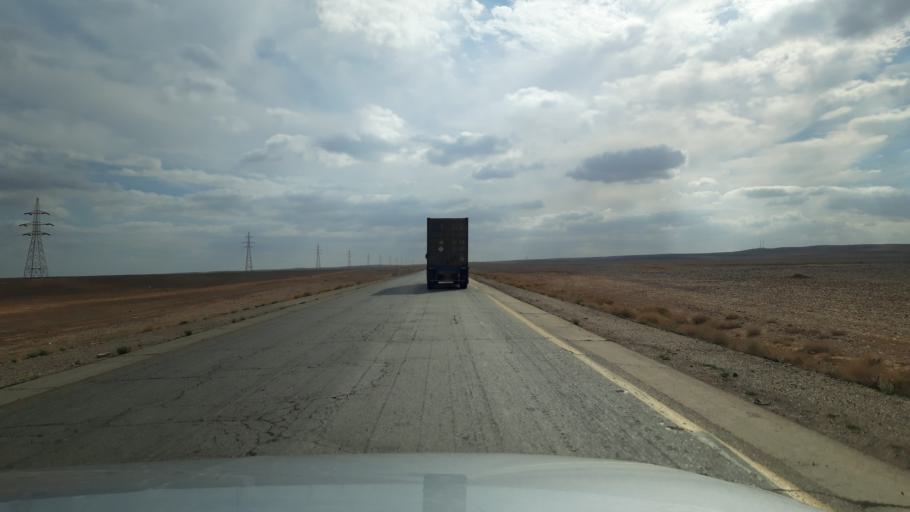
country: JO
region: Amman
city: Al Azraq ash Shamali
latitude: 31.7683
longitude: 36.5607
